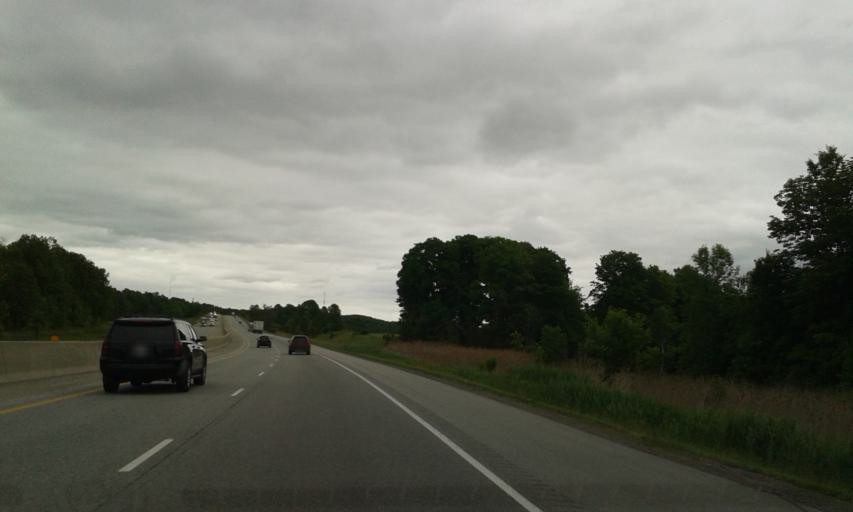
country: CA
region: Ontario
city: Brockville
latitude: 44.5691
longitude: -75.7390
